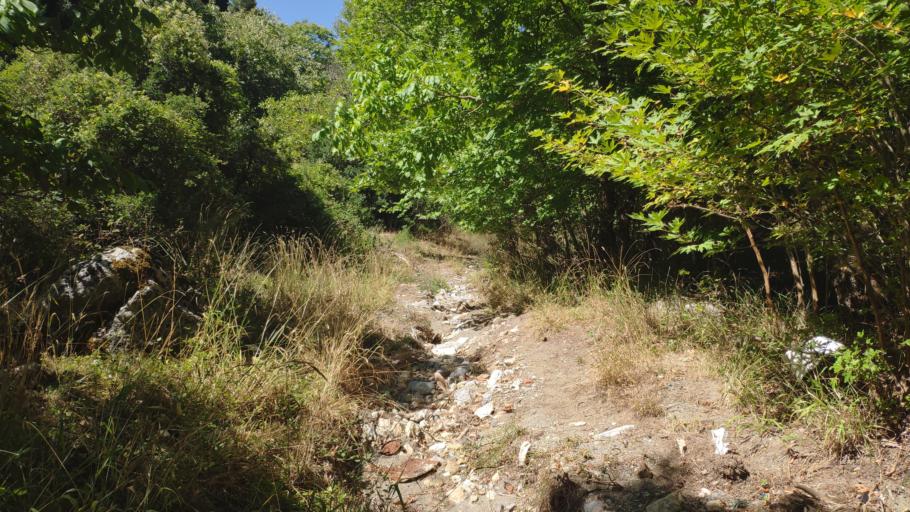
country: GR
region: Peloponnese
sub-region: Nomos Lakonias
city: Kariai
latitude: 37.1761
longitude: 22.5891
